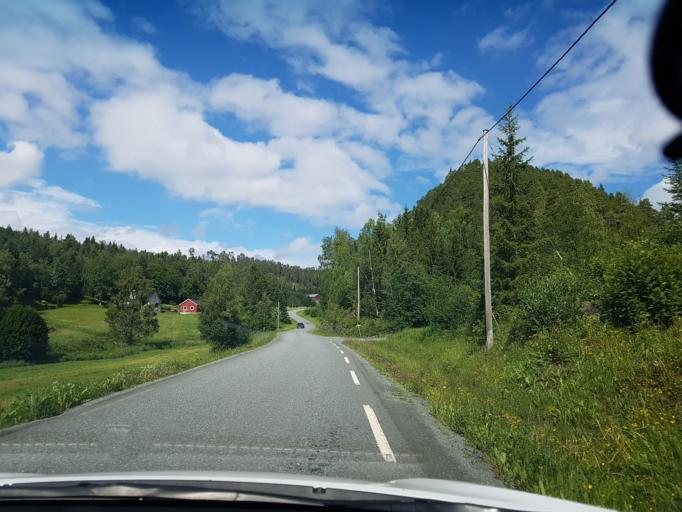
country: NO
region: Nord-Trondelag
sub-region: Frosta
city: Frosta
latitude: 63.6016
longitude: 10.8413
